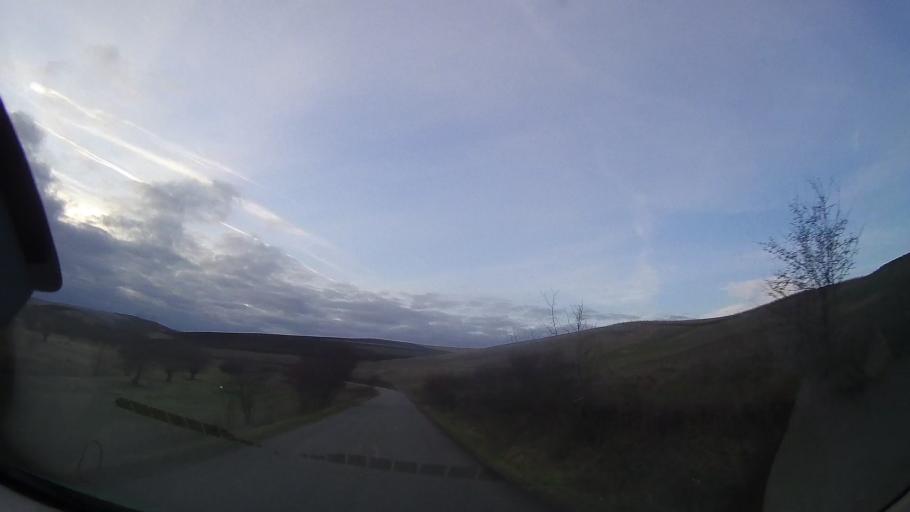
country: RO
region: Cluj
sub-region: Comuna Geaca
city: Geaca
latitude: 46.8531
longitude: 24.0710
